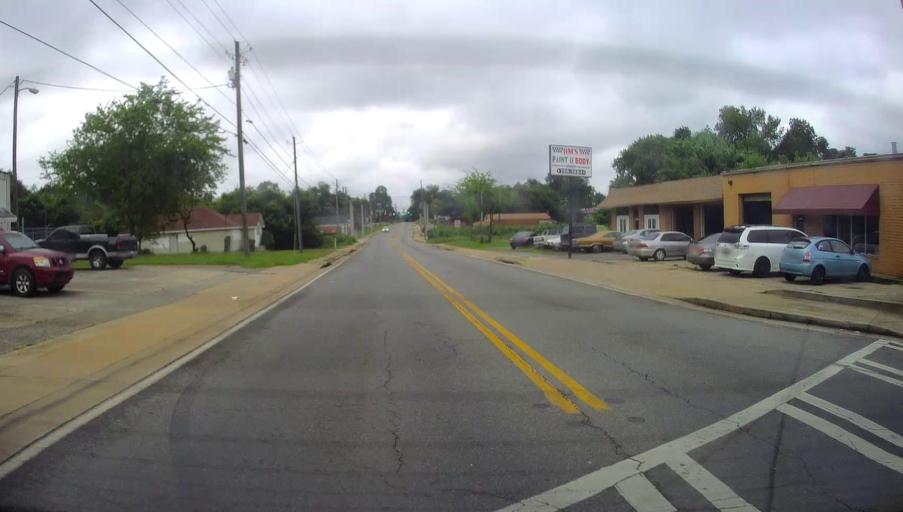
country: US
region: Georgia
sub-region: Bibb County
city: Macon
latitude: 32.7930
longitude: -83.6551
